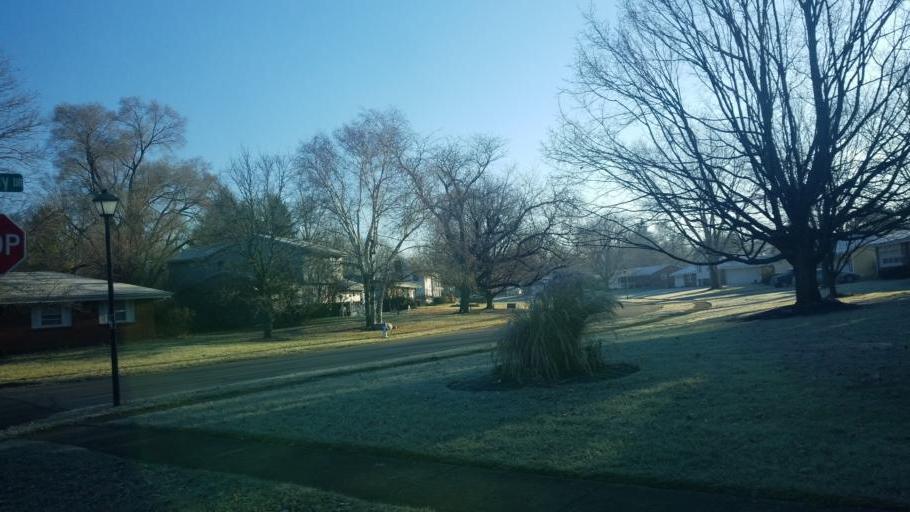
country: US
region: Ohio
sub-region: Marion County
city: Marion
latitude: 40.5728
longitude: -83.1023
